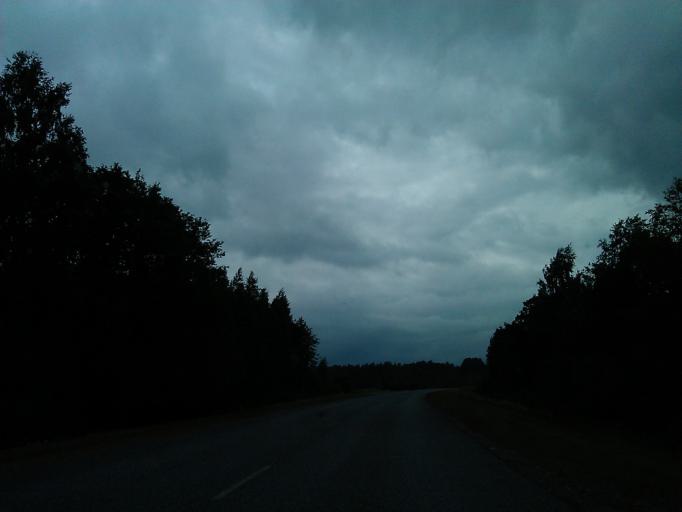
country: LV
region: Kuldigas Rajons
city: Kuldiga
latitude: 56.9857
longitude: 22.0707
